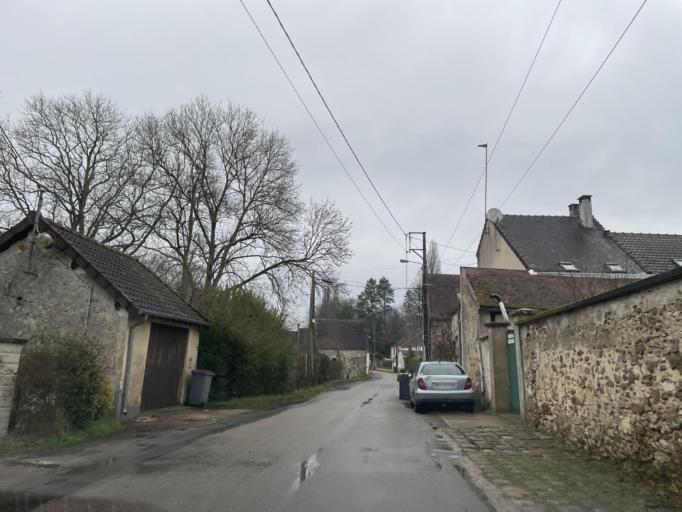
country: FR
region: Ile-de-France
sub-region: Departement de Seine-et-Marne
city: Pommeuse
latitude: 48.8026
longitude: 3.0207
